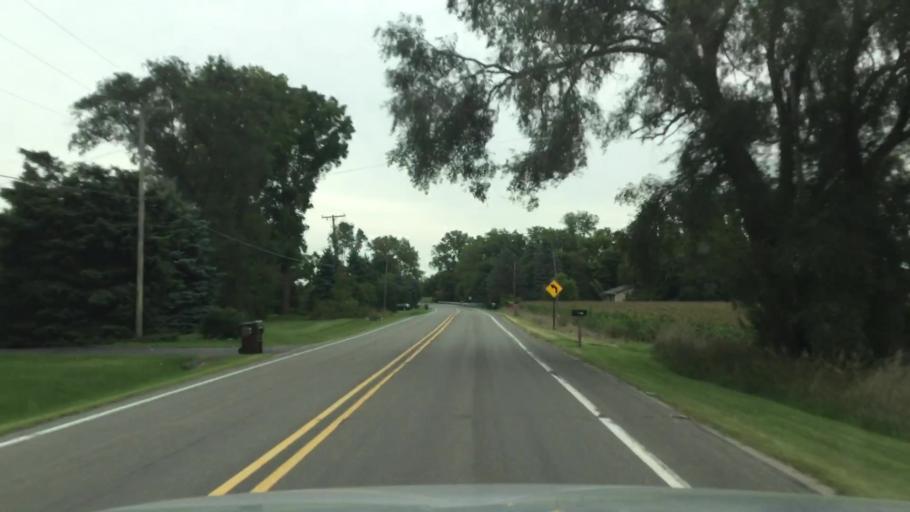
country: US
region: Michigan
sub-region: Washtenaw County
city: Milan
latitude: 42.1254
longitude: -83.6938
